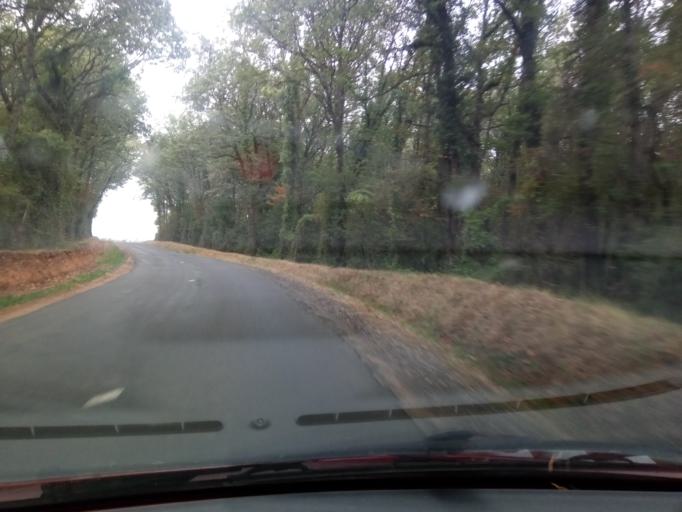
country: FR
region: Poitou-Charentes
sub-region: Departement de la Vienne
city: Saint-Savin
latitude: 46.5240
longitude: 0.7732
